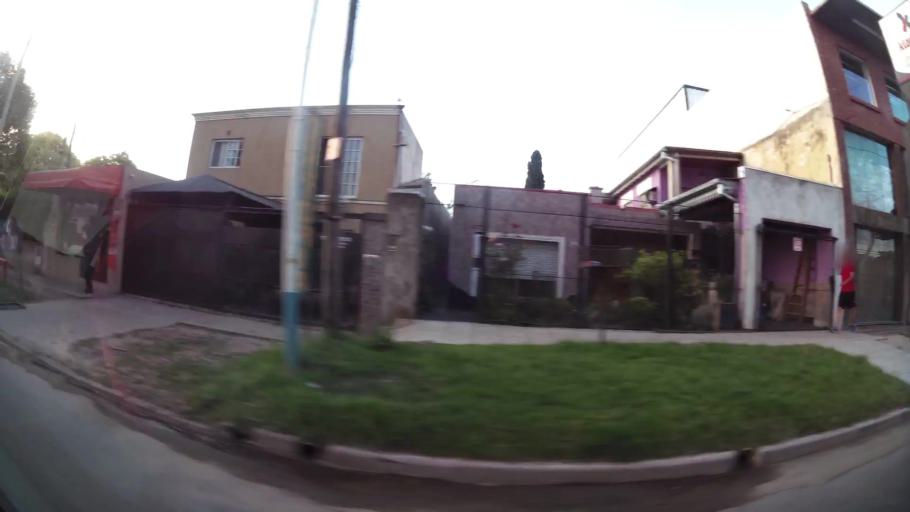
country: AR
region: Buenos Aires
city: Santa Catalina - Dique Lujan
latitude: -34.4726
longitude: -58.7627
